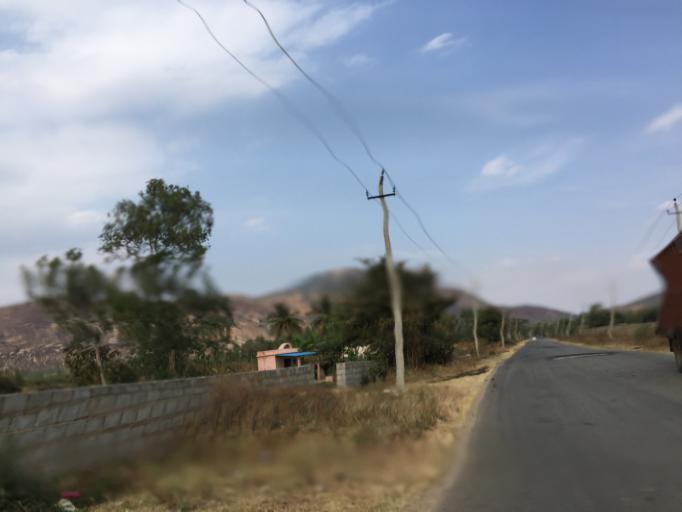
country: IN
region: Karnataka
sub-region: Chikkaballapur
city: Chik Ballapur
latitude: 13.3618
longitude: 77.6541
